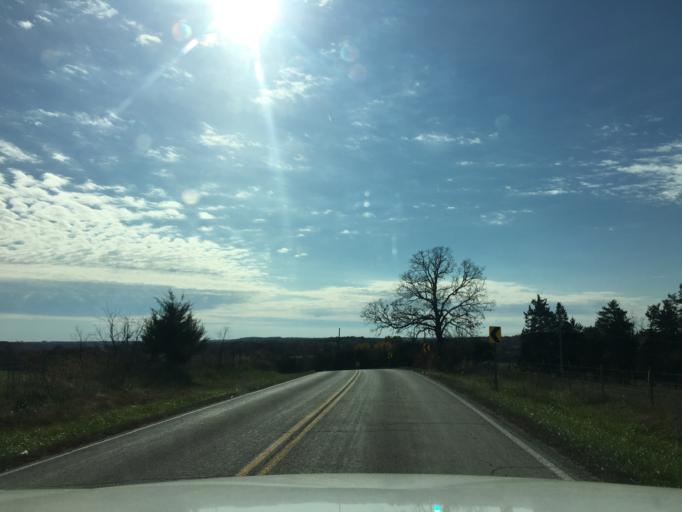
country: US
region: Missouri
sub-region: Osage County
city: Linn
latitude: 38.4095
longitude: -91.8162
